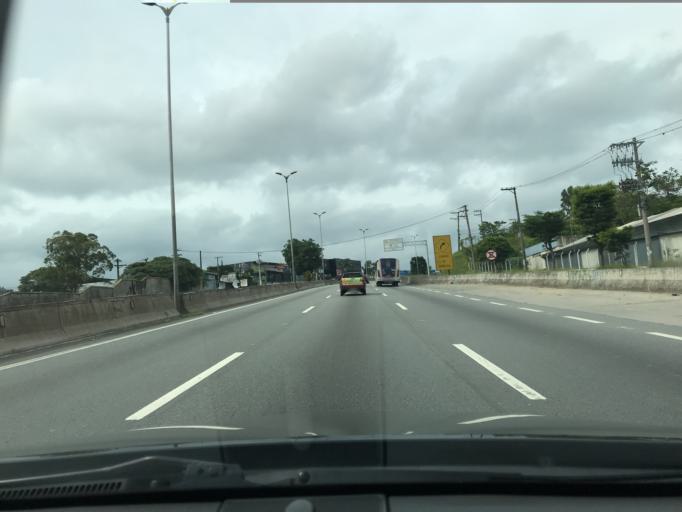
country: BR
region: Sao Paulo
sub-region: Cotia
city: Cotia
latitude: -23.5983
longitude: -46.8814
